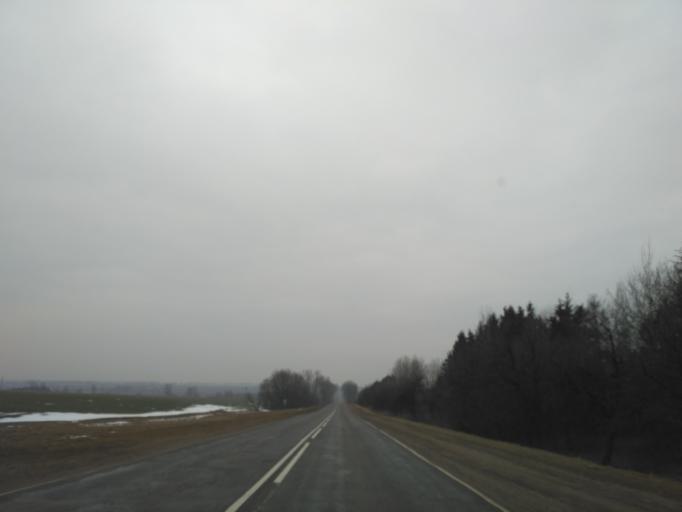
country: BY
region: Minsk
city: Haradzyeya
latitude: 53.3390
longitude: 26.4733
